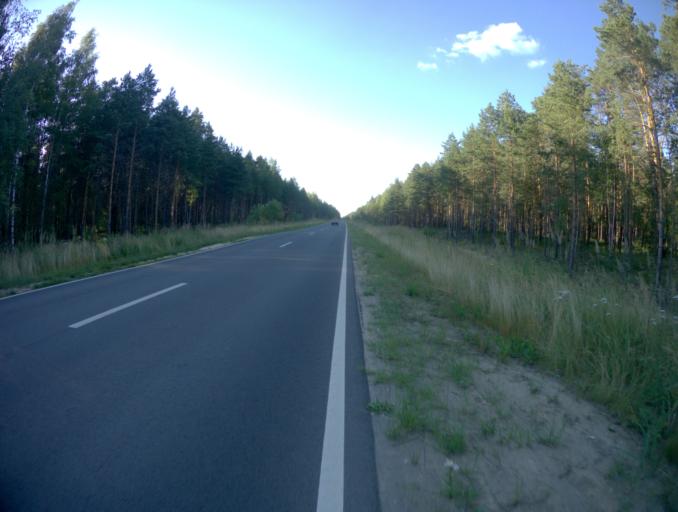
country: RU
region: Vladimir
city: Galitsy
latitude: 56.0490
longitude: 42.8642
